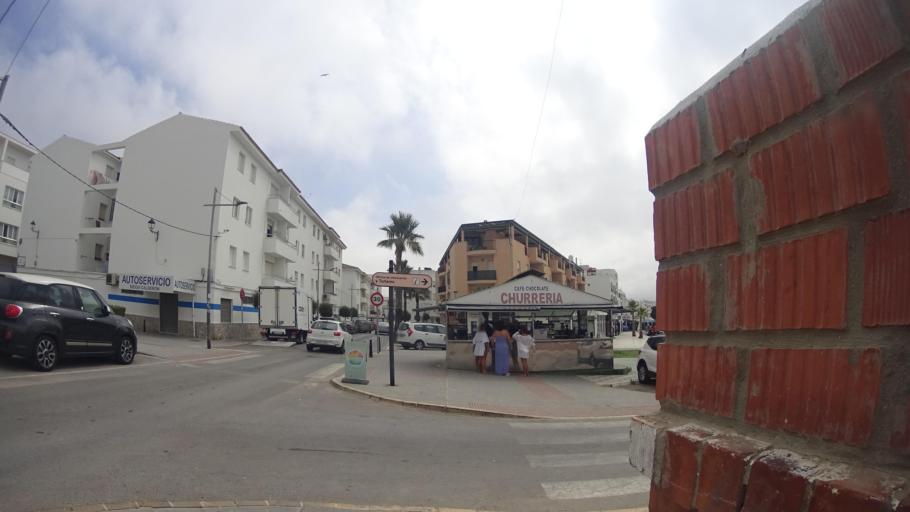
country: ES
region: Andalusia
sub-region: Provincia de Cadiz
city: Barbate de Franco
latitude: 36.1873
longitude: -5.9225
